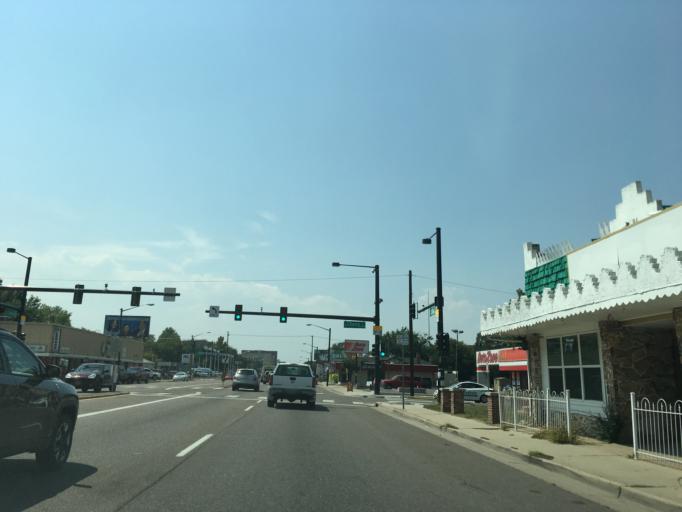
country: US
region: Colorado
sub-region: Arapahoe County
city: Glendale
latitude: 39.7402
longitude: -104.9332
